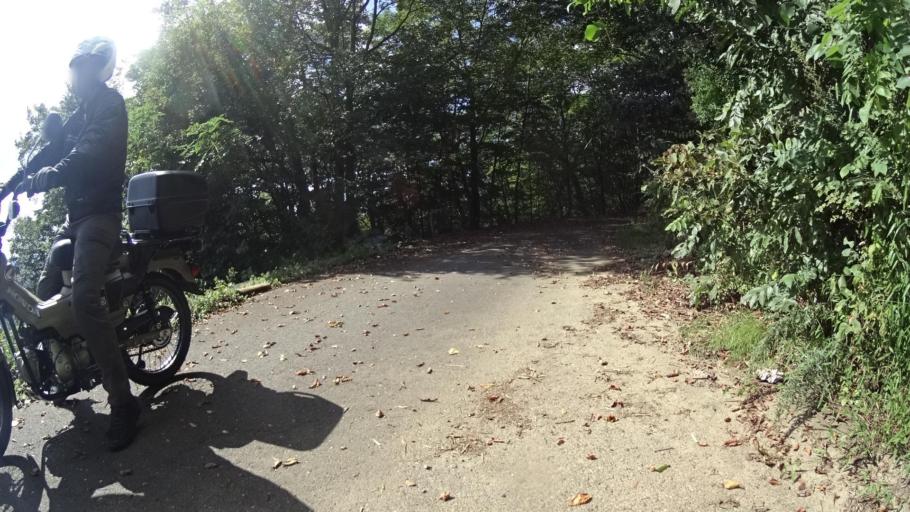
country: JP
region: Yamanashi
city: Uenohara
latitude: 35.7473
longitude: 139.0505
